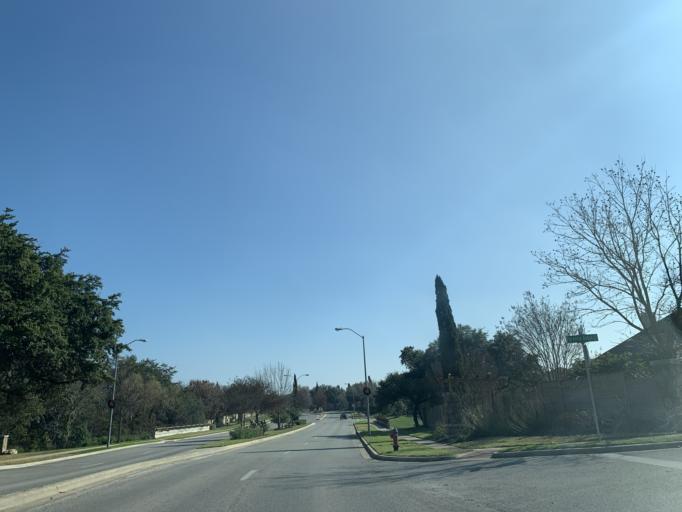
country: US
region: Texas
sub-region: Williamson County
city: Round Rock
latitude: 30.5084
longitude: -97.6284
